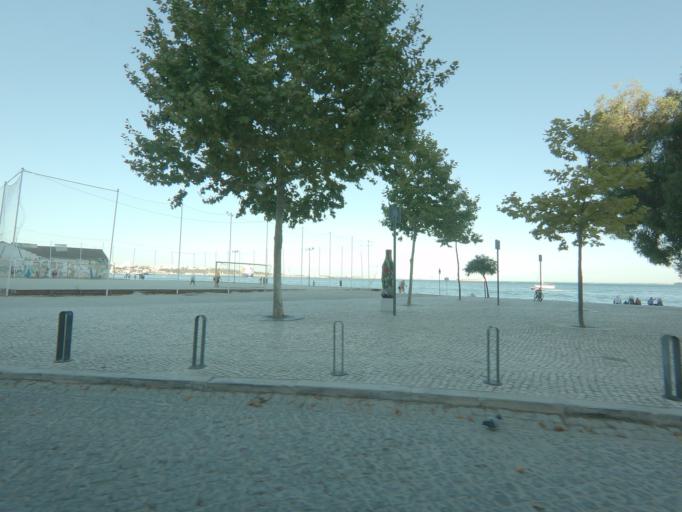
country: PT
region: Setubal
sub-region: Setubal
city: Setubal
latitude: 38.5155
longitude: -8.9086
